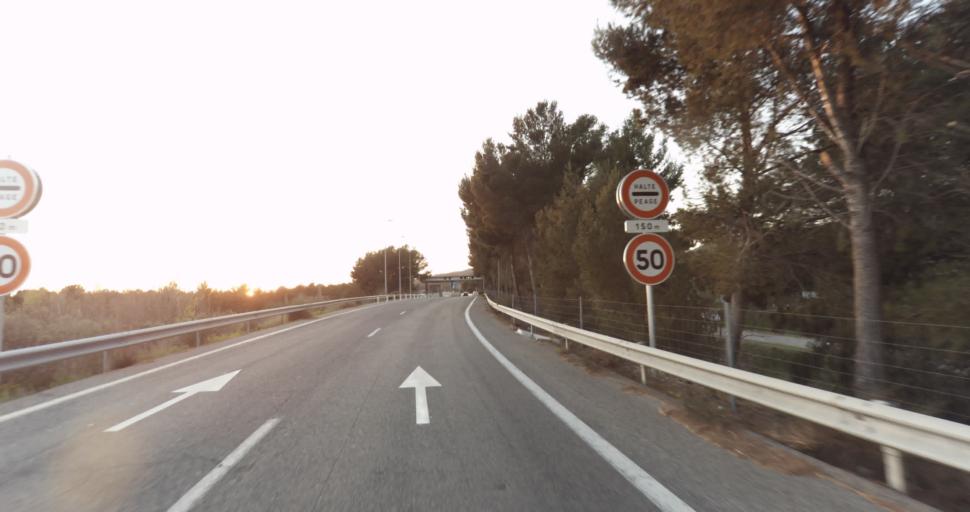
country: FR
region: Provence-Alpes-Cote d'Azur
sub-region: Departement des Bouches-du-Rhone
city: Coudoux
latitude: 43.5524
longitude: 5.2404
